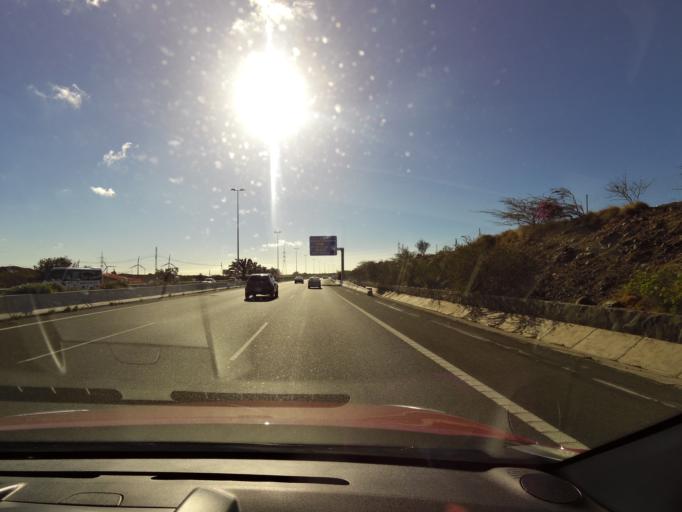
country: ES
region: Canary Islands
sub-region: Provincia de Las Palmas
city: Cruce de Arinaga
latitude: 27.8287
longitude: -15.4483
